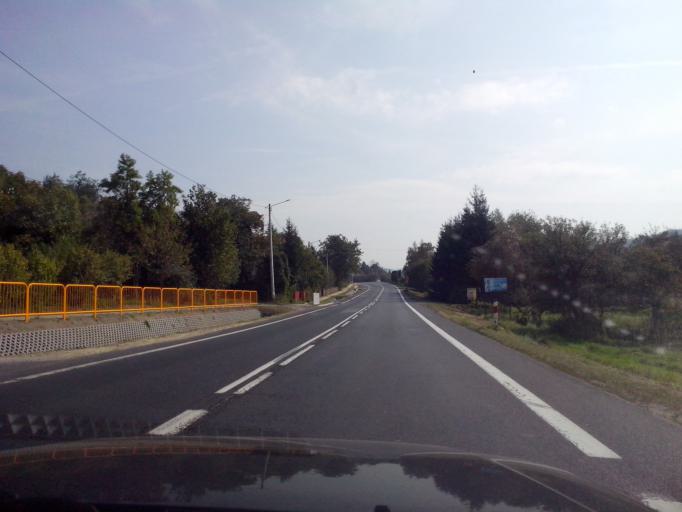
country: PL
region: Subcarpathian Voivodeship
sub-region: Powiat strzyzowski
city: Babica
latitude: 49.9366
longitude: 21.8809
